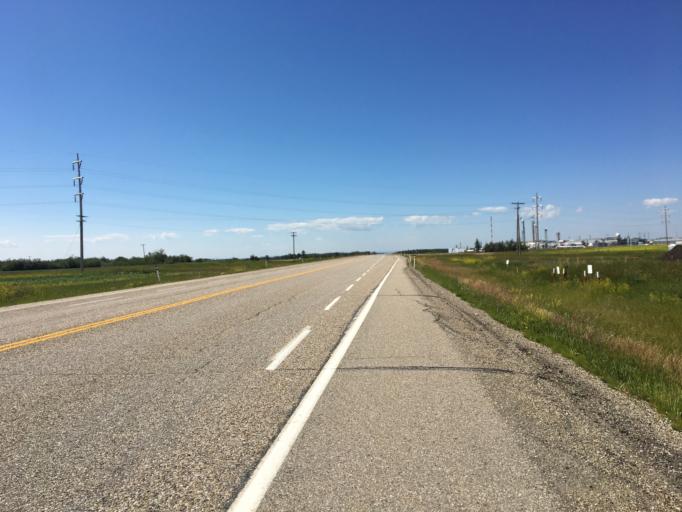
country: CA
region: Alberta
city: Fairview
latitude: 56.0010
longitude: -118.5205
